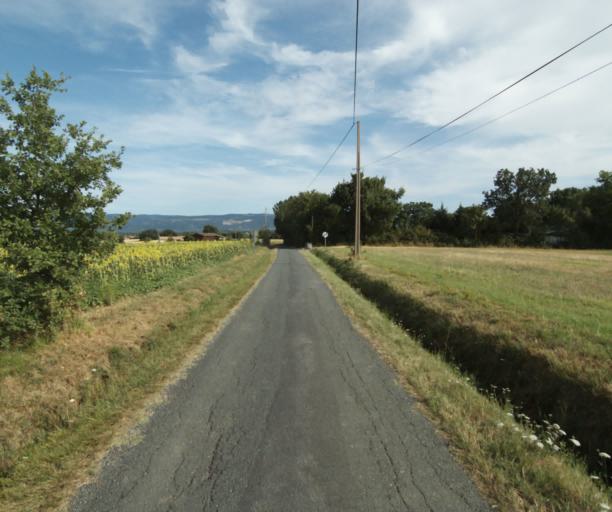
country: FR
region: Midi-Pyrenees
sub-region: Departement du Tarn
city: Soual
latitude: 43.5357
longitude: 2.0649
